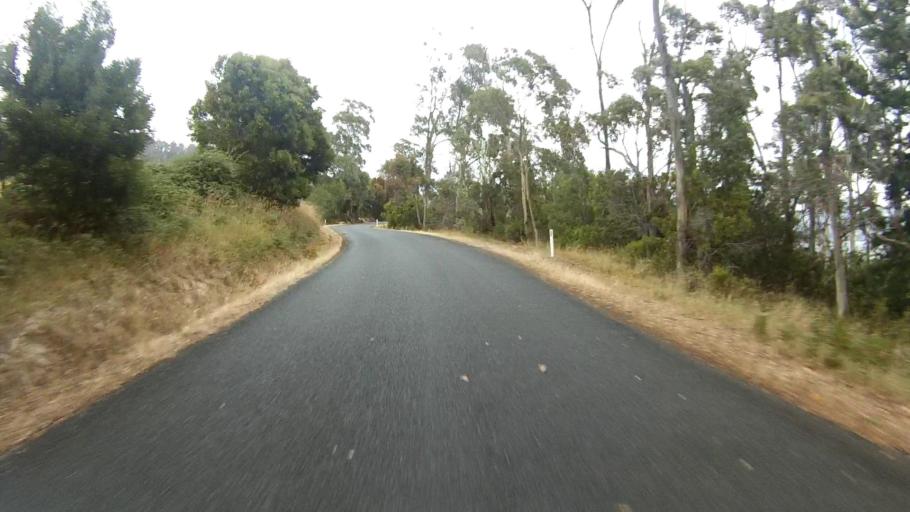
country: AU
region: Tasmania
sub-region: Huon Valley
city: Cygnet
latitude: -43.2144
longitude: 147.1079
